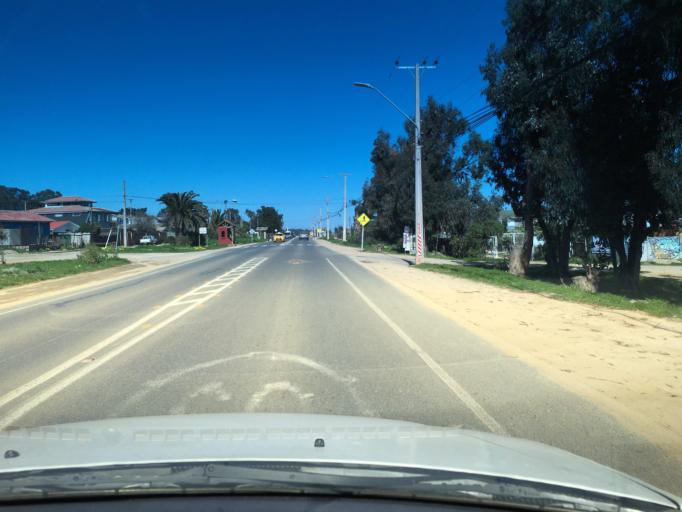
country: CL
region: Valparaiso
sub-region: San Antonio Province
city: El Tabo
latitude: -33.4272
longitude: -71.6907
